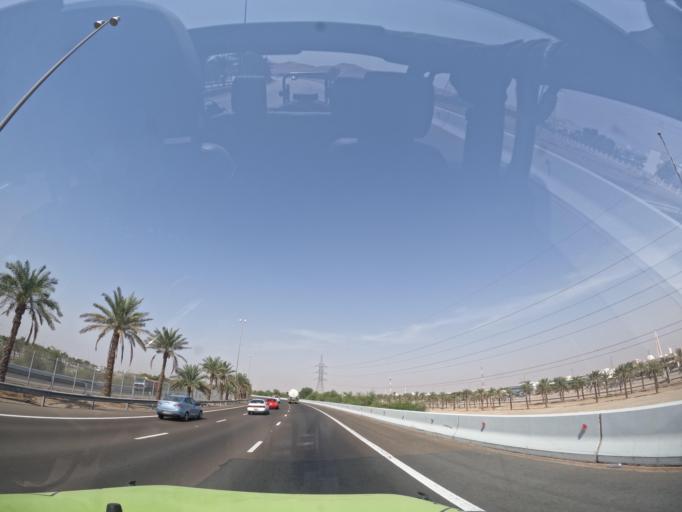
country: AE
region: Abu Dhabi
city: Al Ain
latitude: 24.2245
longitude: 55.5621
